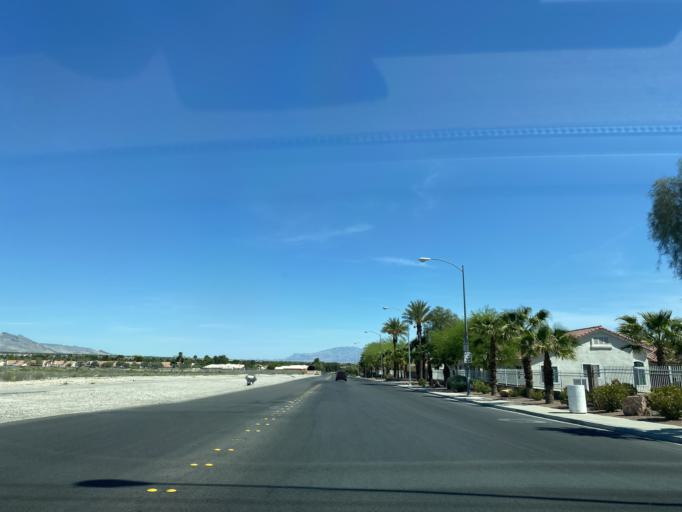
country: US
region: Nevada
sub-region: Clark County
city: Spring Valley
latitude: 36.0850
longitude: -115.2609
